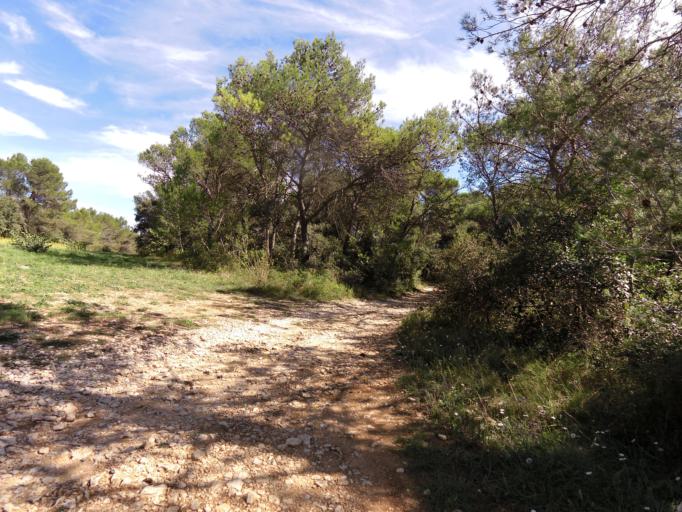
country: FR
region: Languedoc-Roussillon
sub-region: Departement du Gard
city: Vergeze
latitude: 43.7567
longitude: 4.2212
